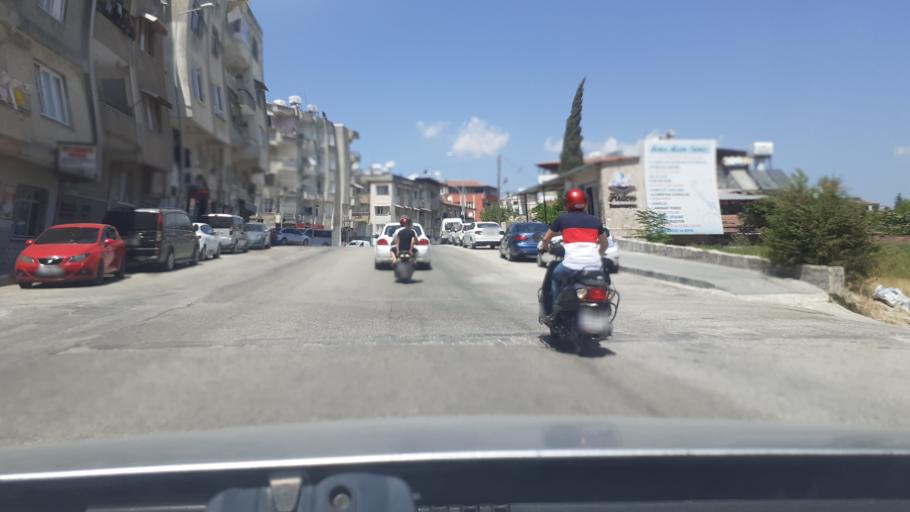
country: TR
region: Hatay
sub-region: Antakya Ilcesi
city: Antakya
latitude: 36.1975
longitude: 36.1549
